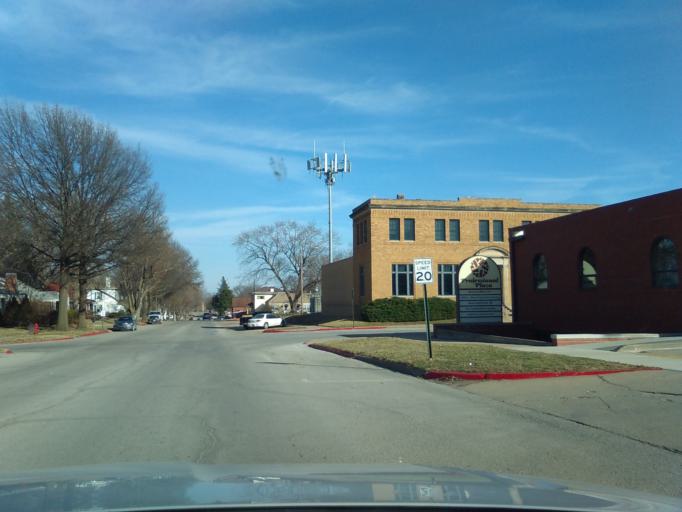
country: US
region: Nebraska
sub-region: Otoe County
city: Nebraska City
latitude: 40.6776
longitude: -95.8581
